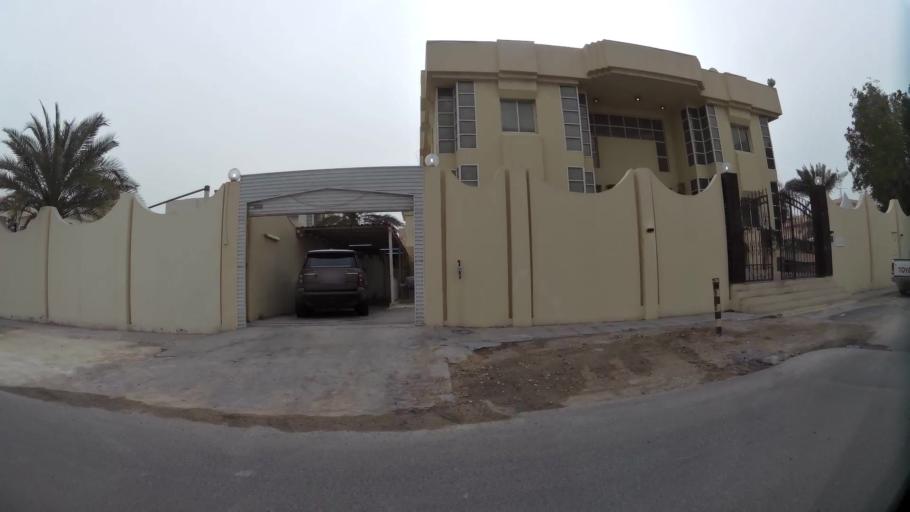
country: QA
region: Baladiyat ad Dawhah
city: Doha
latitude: 25.2591
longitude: 51.4926
